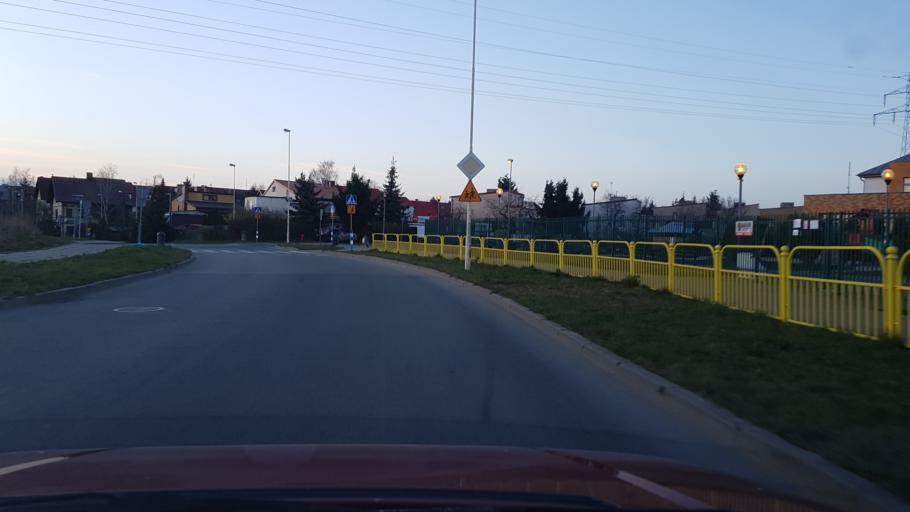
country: PL
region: West Pomeranian Voivodeship
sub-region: Szczecin
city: Szczecin
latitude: 53.4656
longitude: 14.5387
